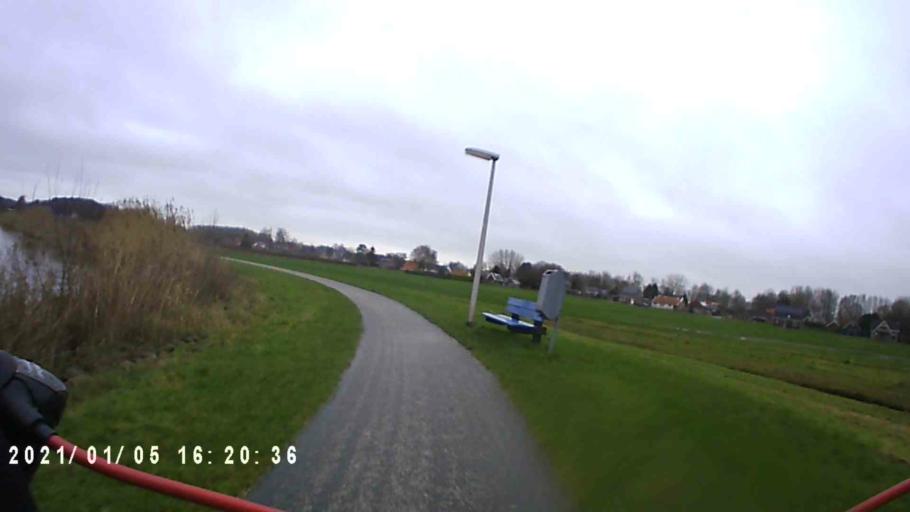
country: NL
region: Groningen
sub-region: Gemeente  Oldambt
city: Winschoten
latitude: 53.1977
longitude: 7.0439
